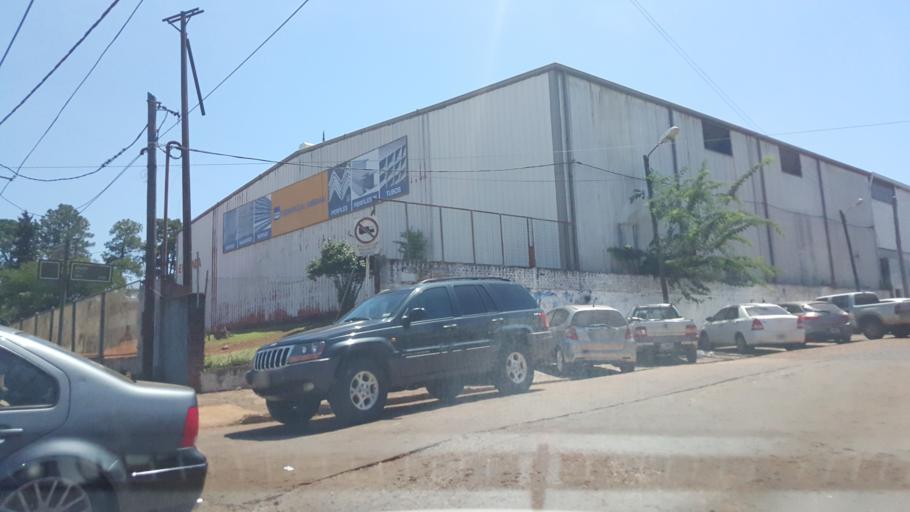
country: AR
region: Misiones
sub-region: Departamento de Capital
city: Posadas
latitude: -27.4003
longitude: -55.9021
